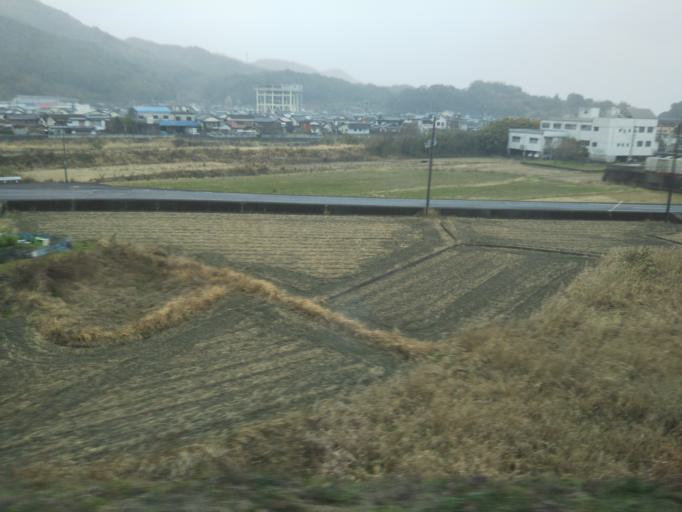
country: JP
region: Kochi
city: Nakamura
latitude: 33.0776
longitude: 133.1029
